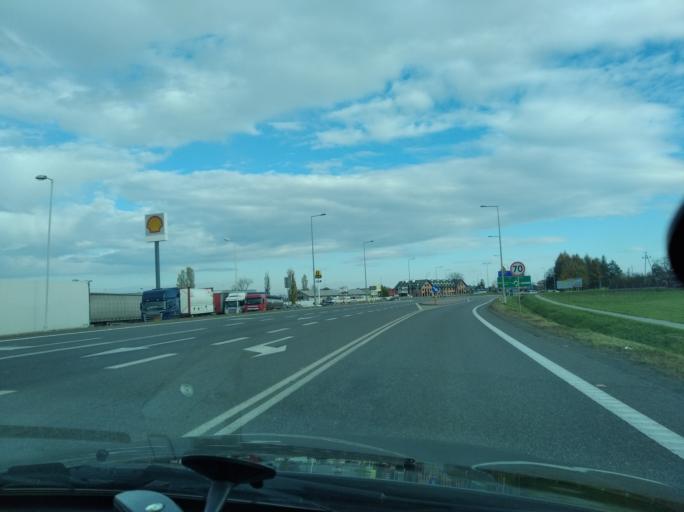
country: PL
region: Subcarpathian Voivodeship
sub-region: Powiat debicki
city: Debica
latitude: 50.0551
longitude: 21.4540
